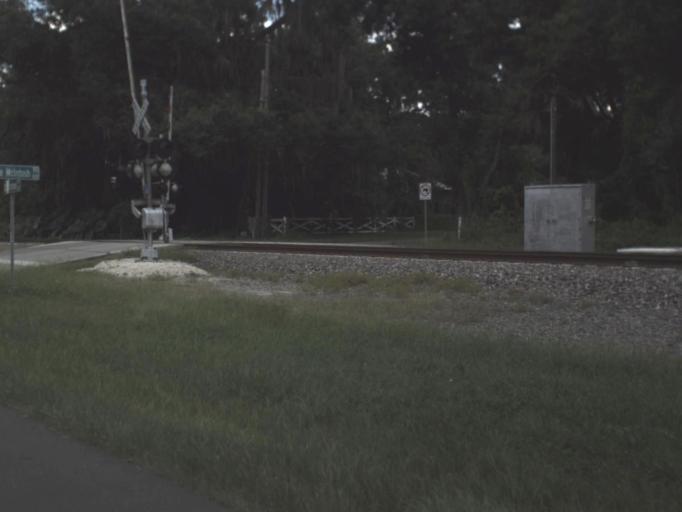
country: US
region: Florida
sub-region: Hillsborough County
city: Plant City
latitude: 28.0512
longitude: -82.1307
